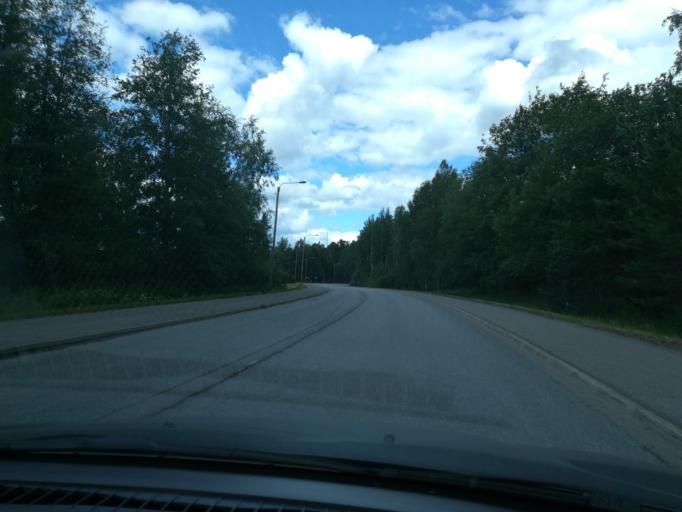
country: FI
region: Southern Savonia
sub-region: Mikkeli
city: Maentyharju
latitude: 61.4116
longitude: 26.8843
